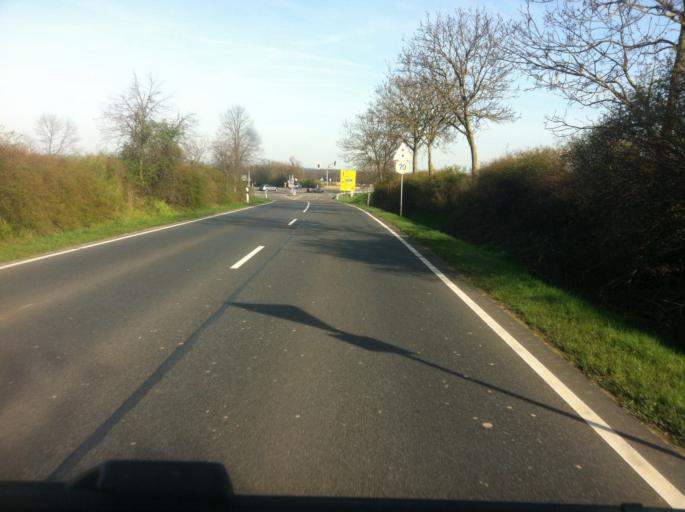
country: DE
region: North Rhine-Westphalia
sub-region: Regierungsbezirk Koln
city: Vettweiss
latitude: 50.7372
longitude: 6.5493
